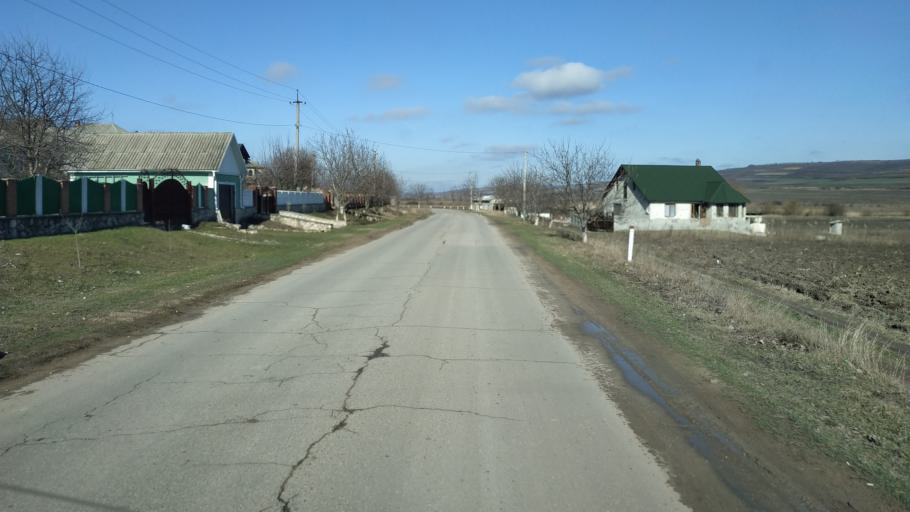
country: MD
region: Hincesti
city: Hincesti
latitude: 46.9366
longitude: 28.6377
